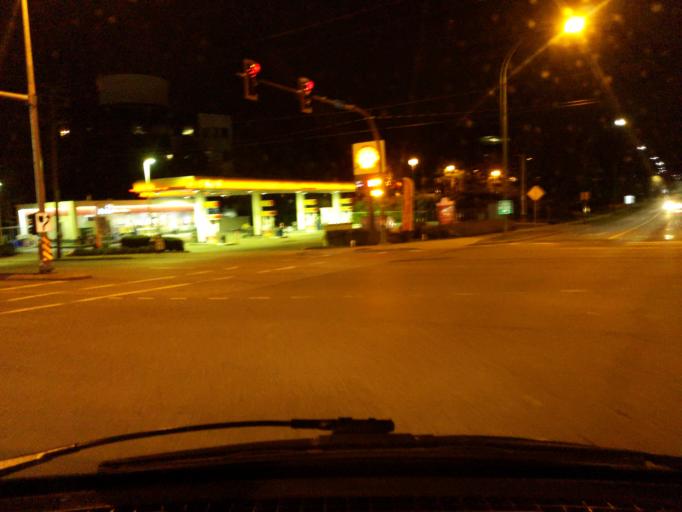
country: CA
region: British Columbia
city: Burnaby
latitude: 49.2547
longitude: -123.0044
